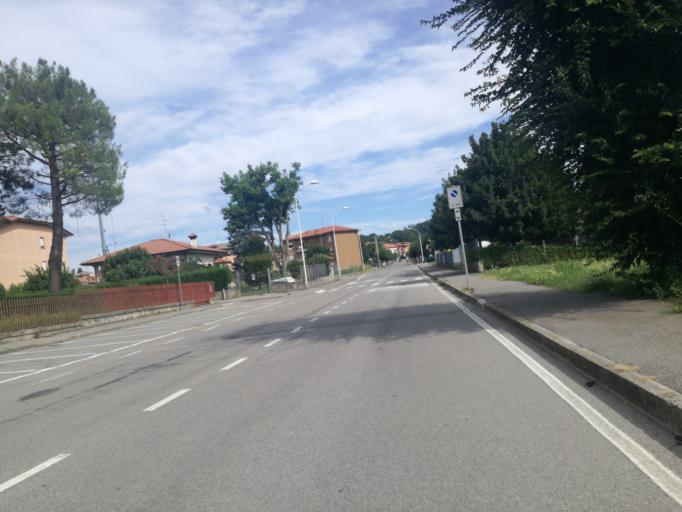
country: IT
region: Lombardy
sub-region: Provincia di Bergamo
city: Calusco d'Adda
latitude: 45.6908
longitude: 9.4658
